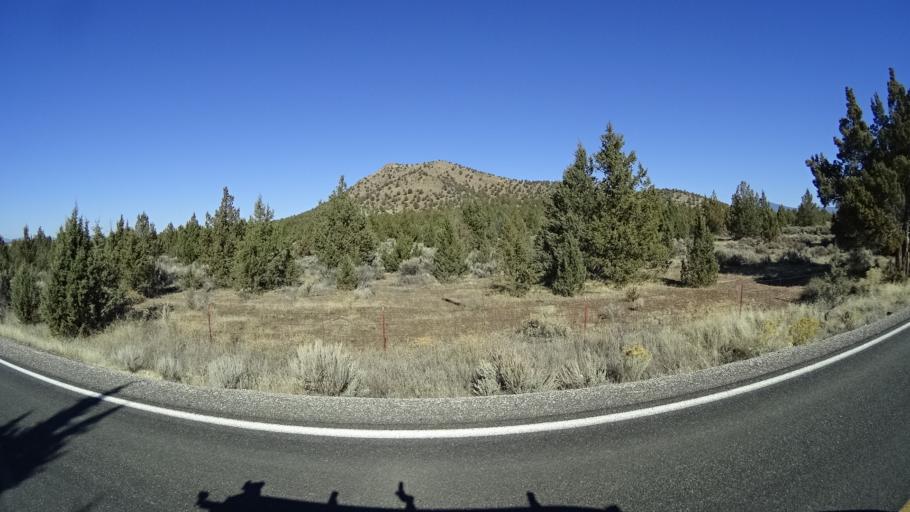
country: US
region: California
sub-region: Siskiyou County
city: Montague
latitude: 41.6600
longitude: -122.3843
